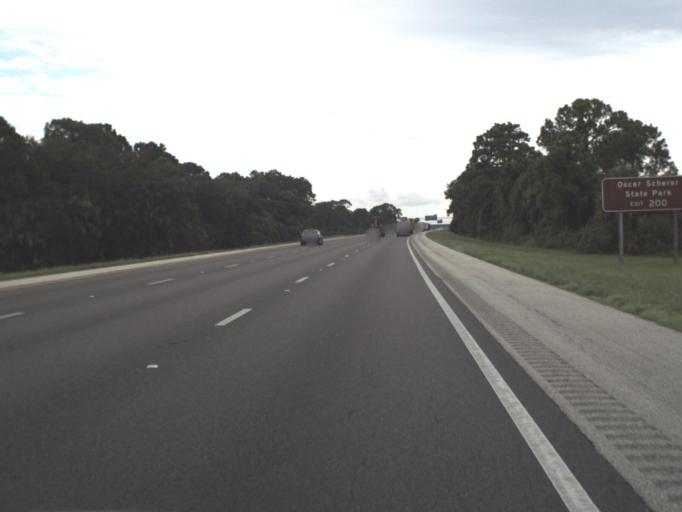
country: US
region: Florida
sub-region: Sarasota County
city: Osprey
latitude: 27.2061
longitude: -82.4429
